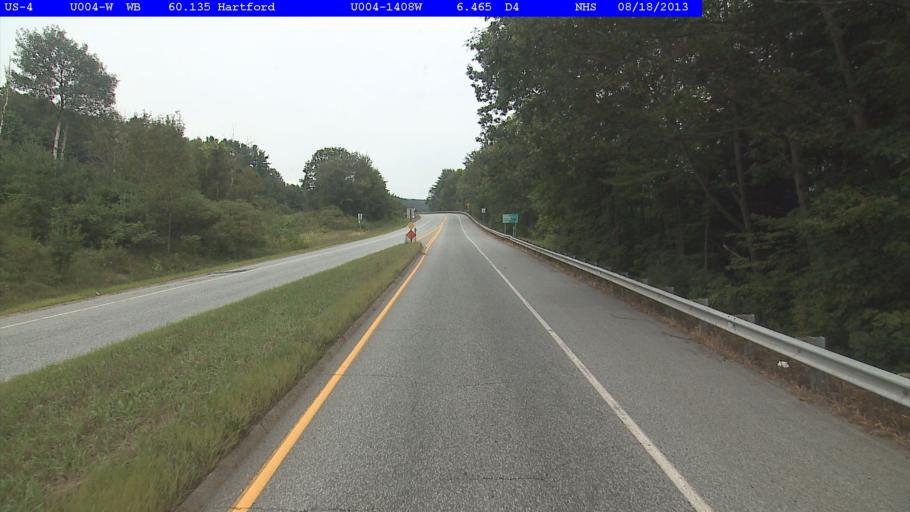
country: US
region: Vermont
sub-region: Windsor County
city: White River Junction
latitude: 43.6661
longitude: -72.3823
